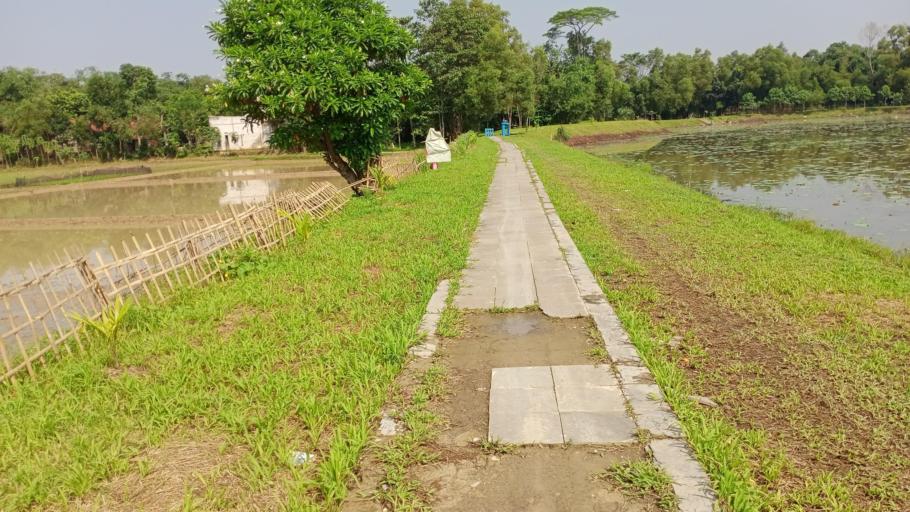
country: ID
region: West Java
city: Cileungsir
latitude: -6.3980
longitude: 107.0843
